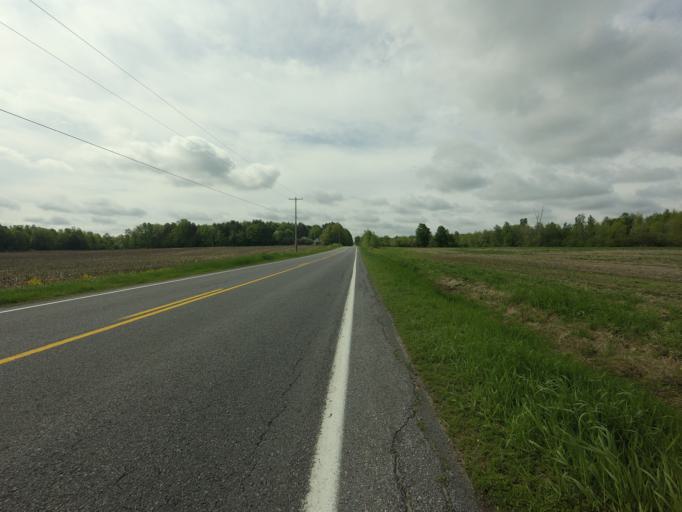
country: CA
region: Ontario
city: Cornwall
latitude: 44.7481
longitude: -74.6678
